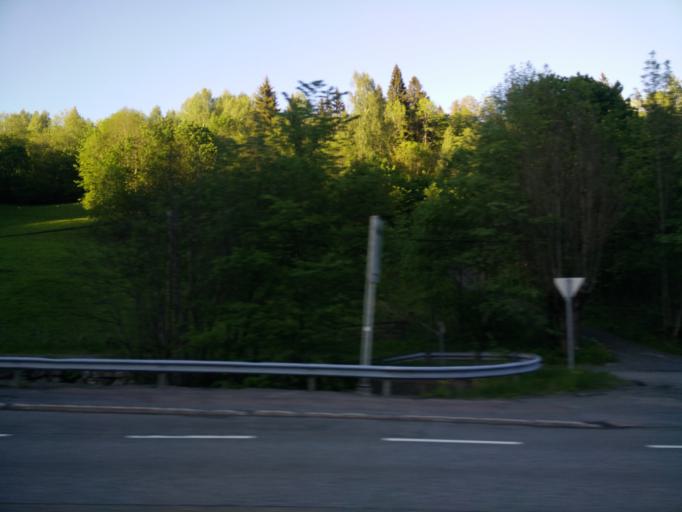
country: NO
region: Akershus
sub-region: Baerum
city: Skui
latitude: 59.9407
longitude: 10.4057
